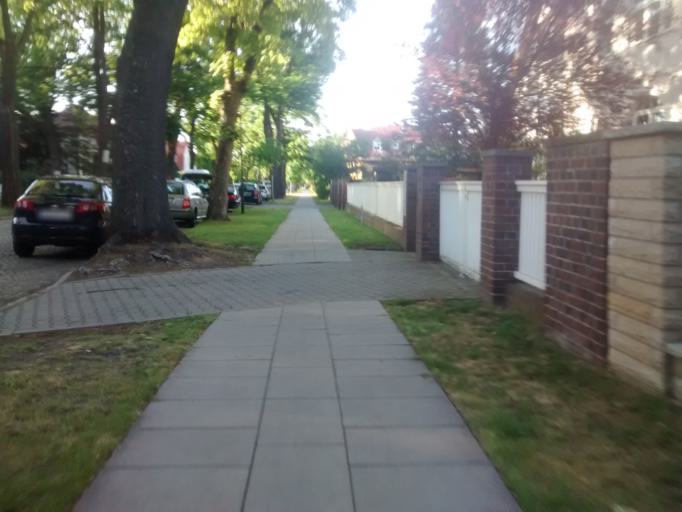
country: DE
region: Brandenburg
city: Hohen Neuendorf
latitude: 52.6714
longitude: 13.2887
